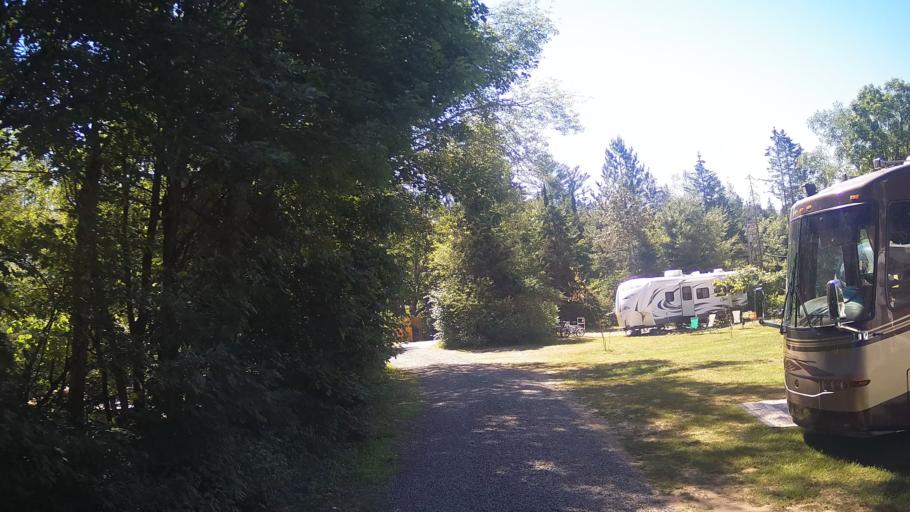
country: CA
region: Ontario
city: Huntsville
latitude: 45.3775
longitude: -79.2154
